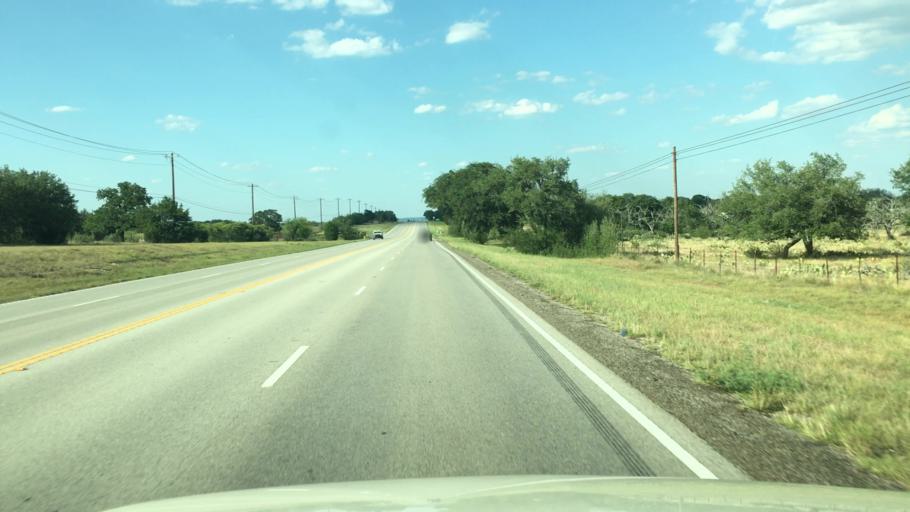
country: US
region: Texas
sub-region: Llano County
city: Horseshoe Bay
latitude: 30.4911
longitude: -98.3103
